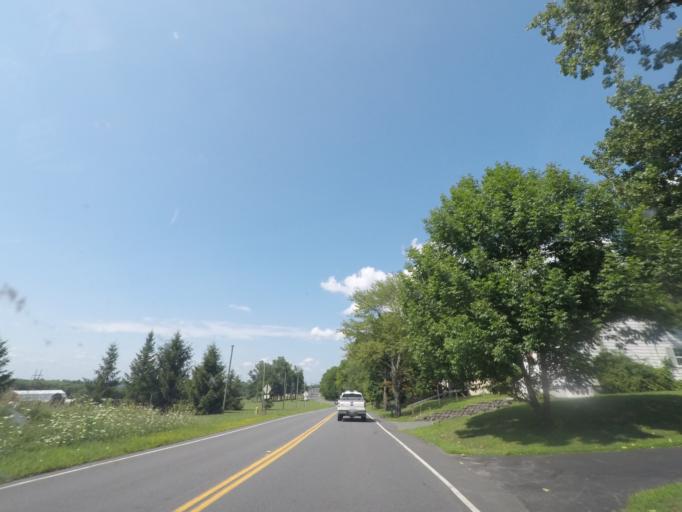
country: US
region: New York
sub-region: Albany County
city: Menands
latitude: 42.6674
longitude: -73.6874
